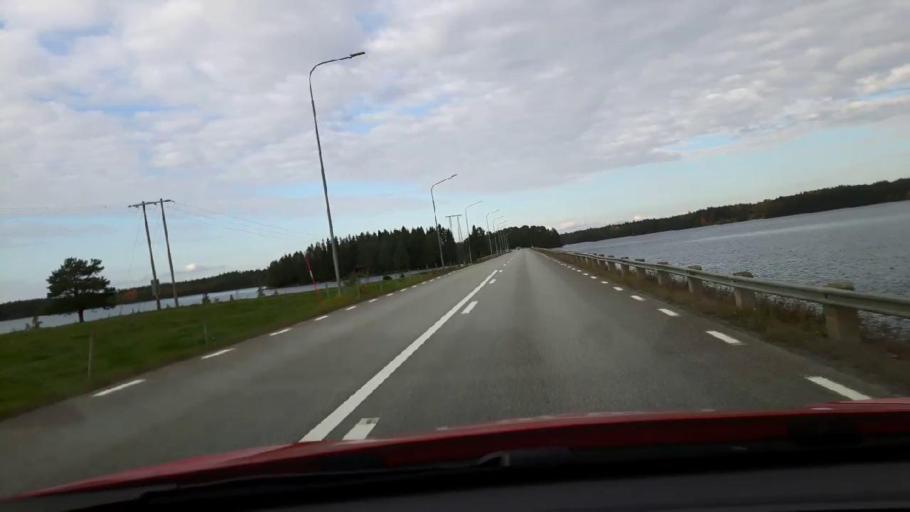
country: SE
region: Jaemtland
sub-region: Krokoms Kommun
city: Valla
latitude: 63.2451
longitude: 13.9993
